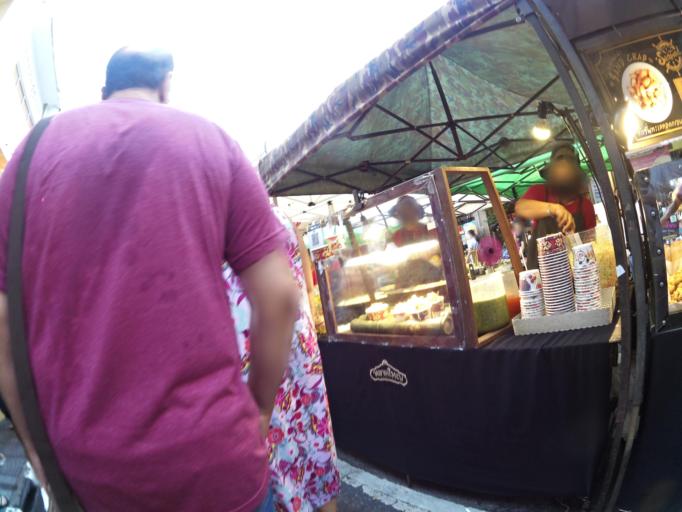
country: TH
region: Phuket
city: Ban Talat Nua
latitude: 7.8848
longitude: 98.3888
